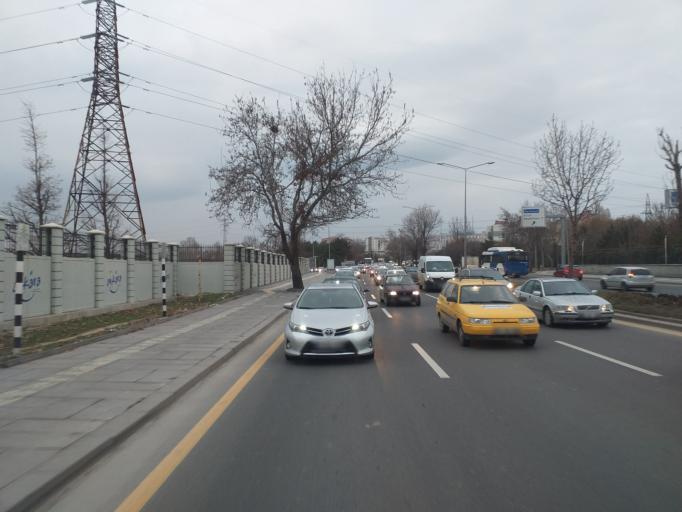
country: TR
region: Ankara
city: Ankara
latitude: 39.9519
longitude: 32.8227
